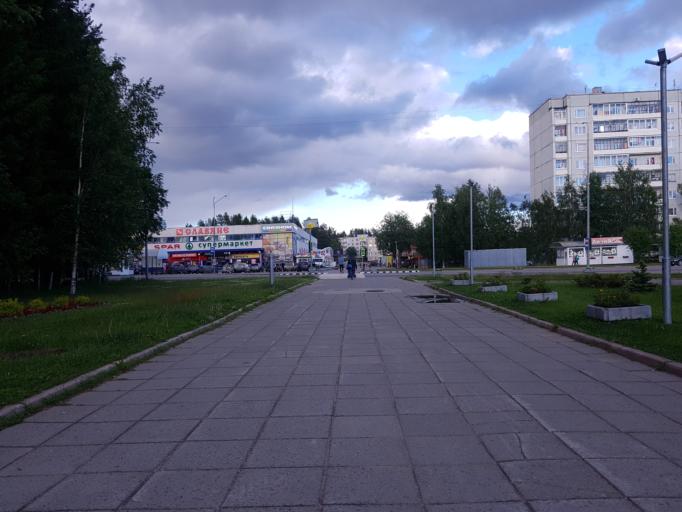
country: RU
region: Republic of Karelia
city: Kostomuksha
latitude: 64.5884
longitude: 30.5978
